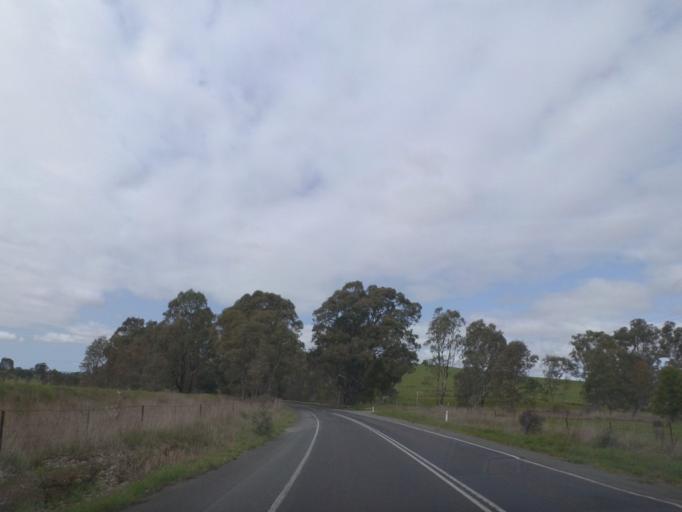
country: AU
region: Victoria
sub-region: Murrindindi
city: Kinglake West
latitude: -37.1637
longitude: 145.2929
